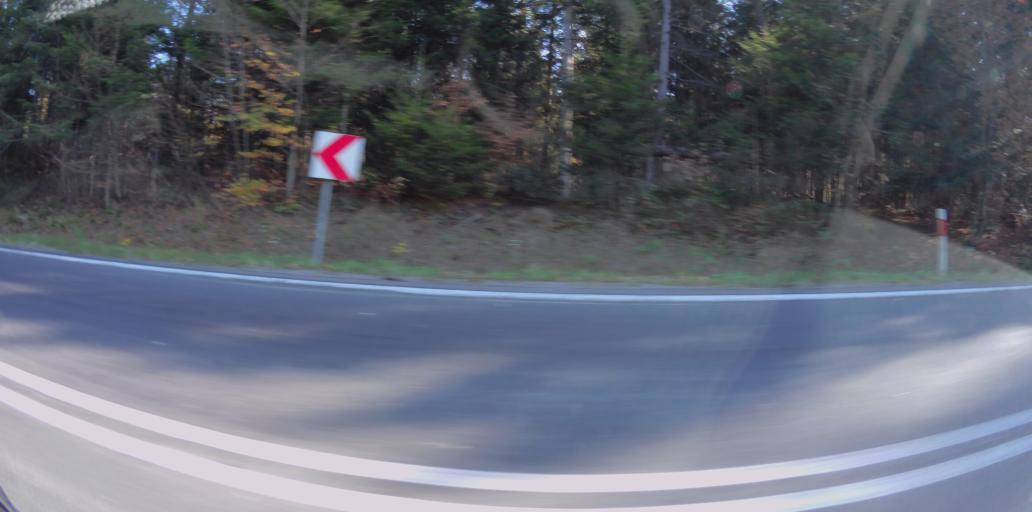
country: PL
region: Subcarpathian Voivodeship
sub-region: Powiat bieszczadzki
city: Ustrzyki Dolne
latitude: 49.5205
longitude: 22.6047
